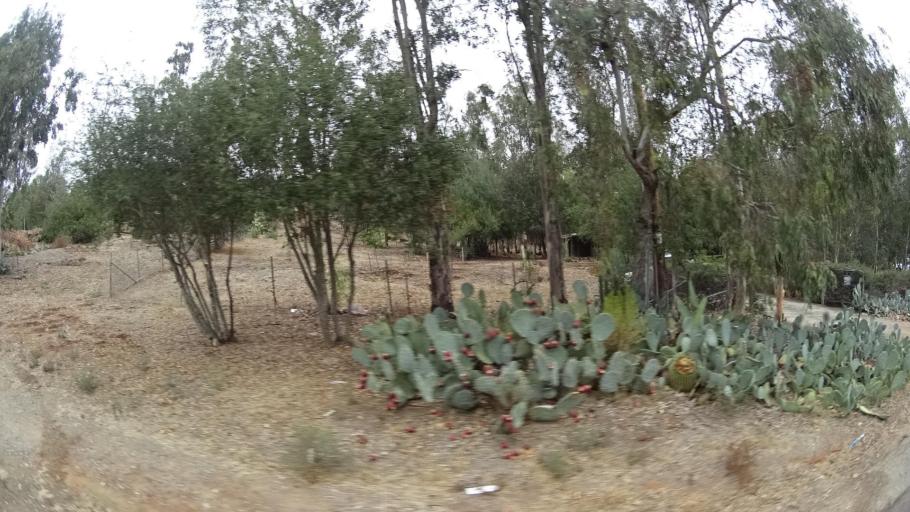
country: US
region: California
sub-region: San Diego County
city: Rancho Santa Fe
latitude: 33.0738
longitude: -117.1663
